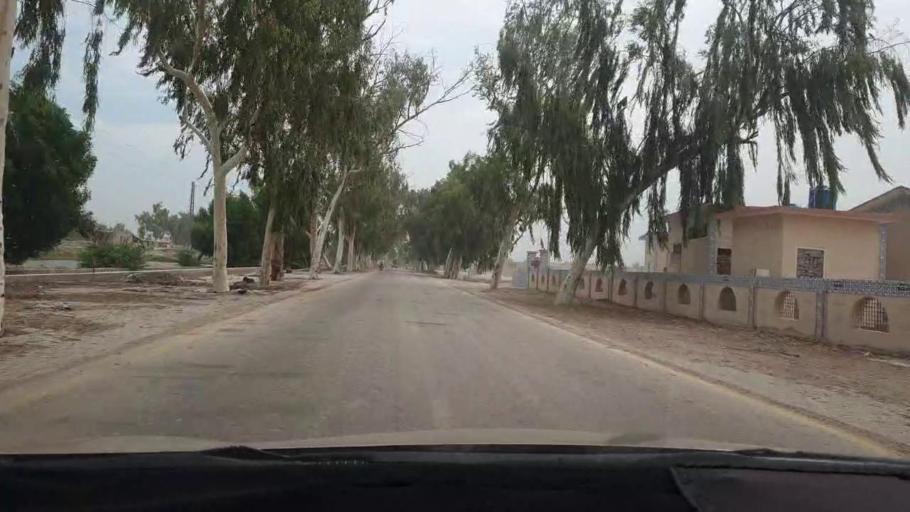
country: PK
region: Sindh
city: Naudero
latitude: 27.6678
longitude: 68.3519
